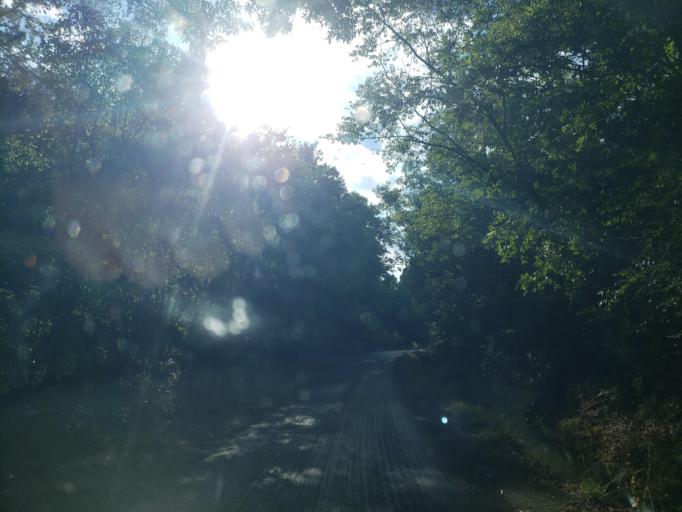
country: US
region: Georgia
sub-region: Floyd County
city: Lindale
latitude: 34.2150
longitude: -85.1278
